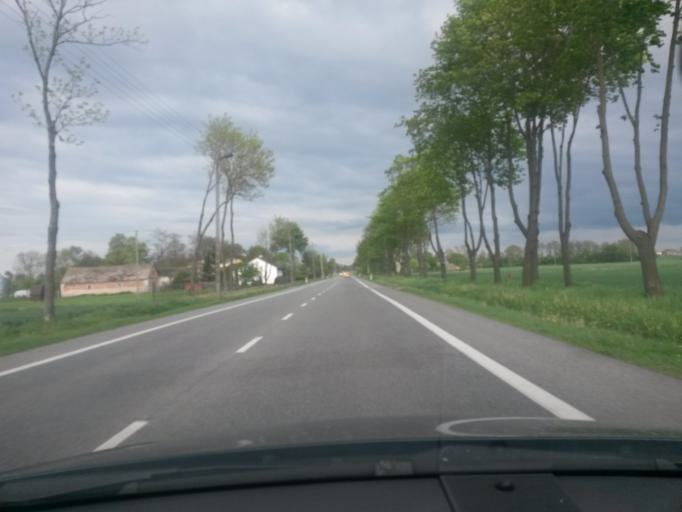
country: PL
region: Masovian Voivodeship
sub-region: Powiat plonski
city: Dzierzaznia
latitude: 52.6277
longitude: 20.2384
